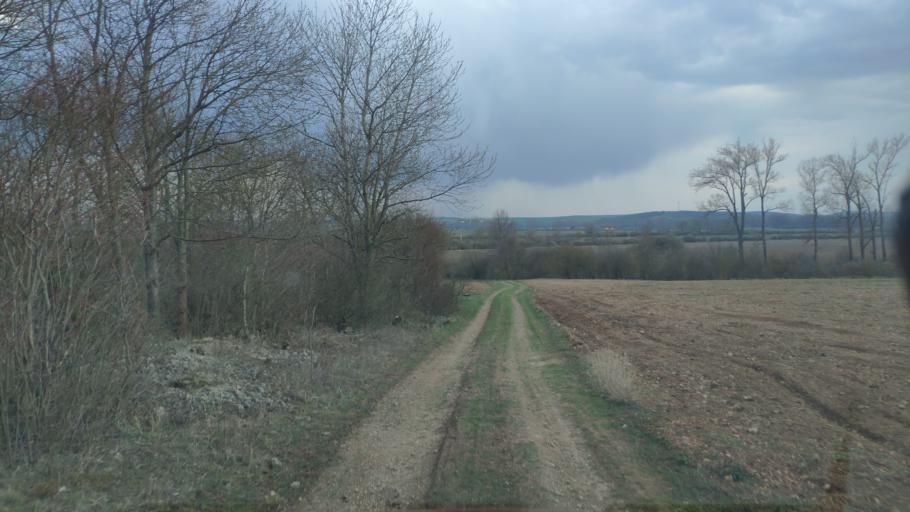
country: SK
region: Kosicky
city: Moldava nad Bodvou
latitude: 48.6170
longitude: 20.9223
